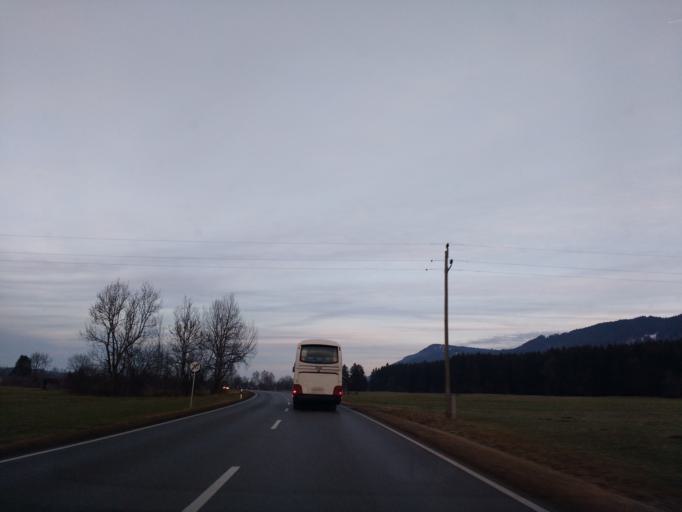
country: DE
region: Bavaria
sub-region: Swabia
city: Schwangau
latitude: 47.5864
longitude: 10.7640
